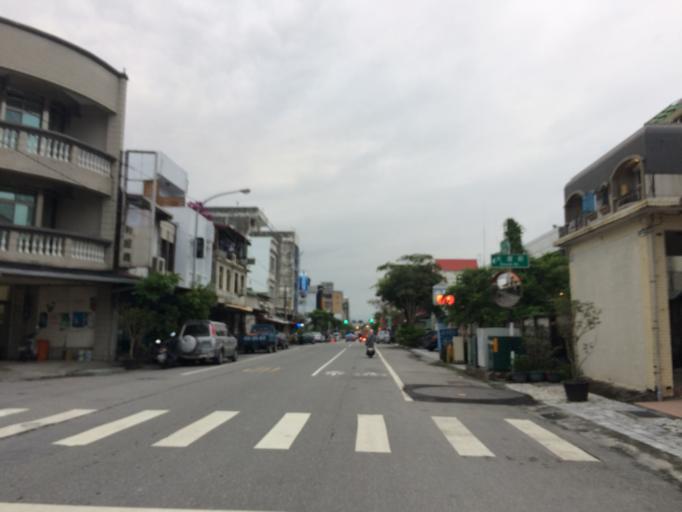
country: TW
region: Taiwan
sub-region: Hualien
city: Hualian
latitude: 23.9750
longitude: 121.6150
